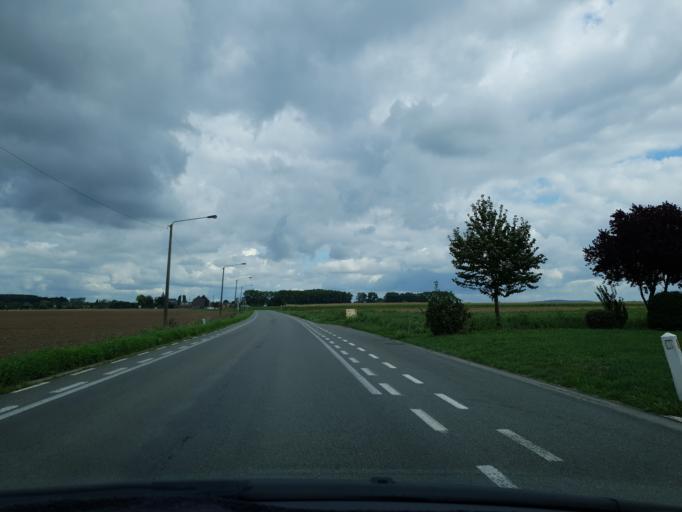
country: BE
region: Wallonia
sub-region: Province du Hainaut
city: Pecq
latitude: 50.7094
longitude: 3.3501
